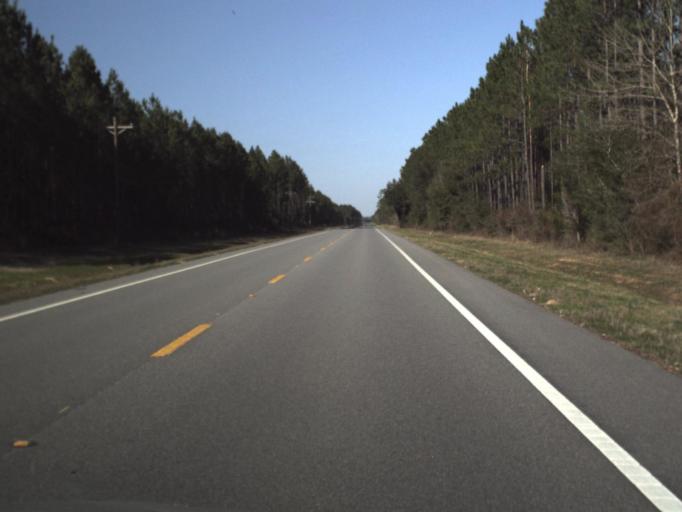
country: US
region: Florida
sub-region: Gulf County
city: Wewahitchka
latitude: 30.2953
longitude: -85.2390
